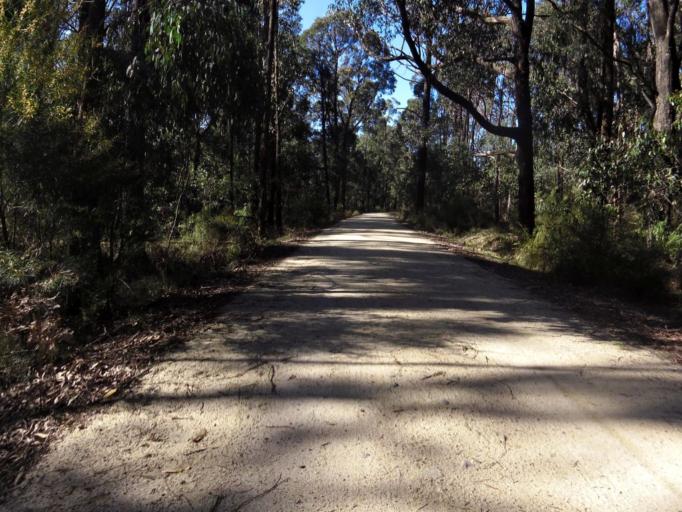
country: AU
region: Victoria
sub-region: Latrobe
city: Moe
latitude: -38.3776
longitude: 146.1952
